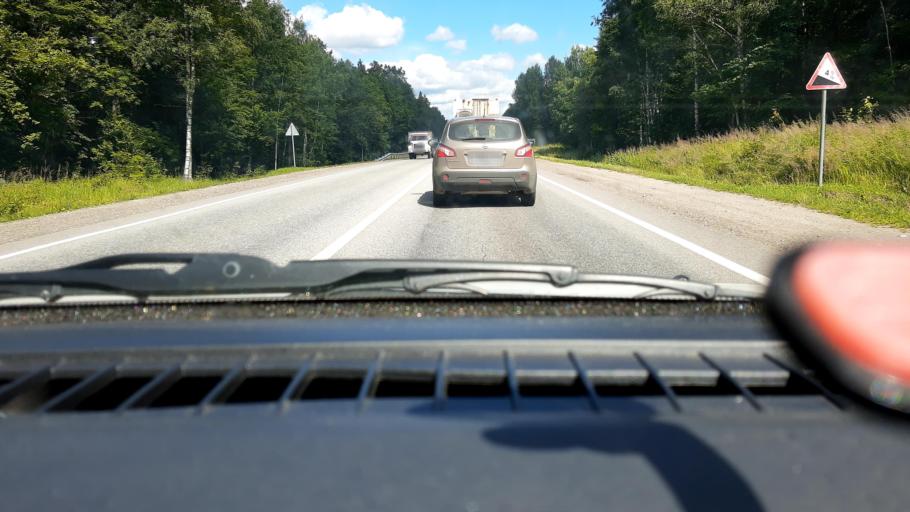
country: RU
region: Nizjnij Novgorod
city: Surovatikha
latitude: 55.6831
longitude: 43.9903
